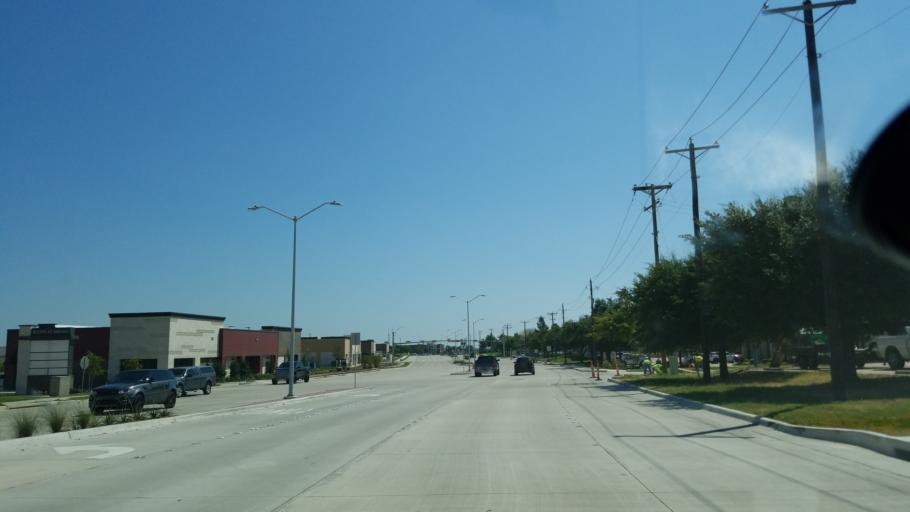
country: US
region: Texas
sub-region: Tarrant County
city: Mansfield
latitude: 32.5690
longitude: -97.1148
